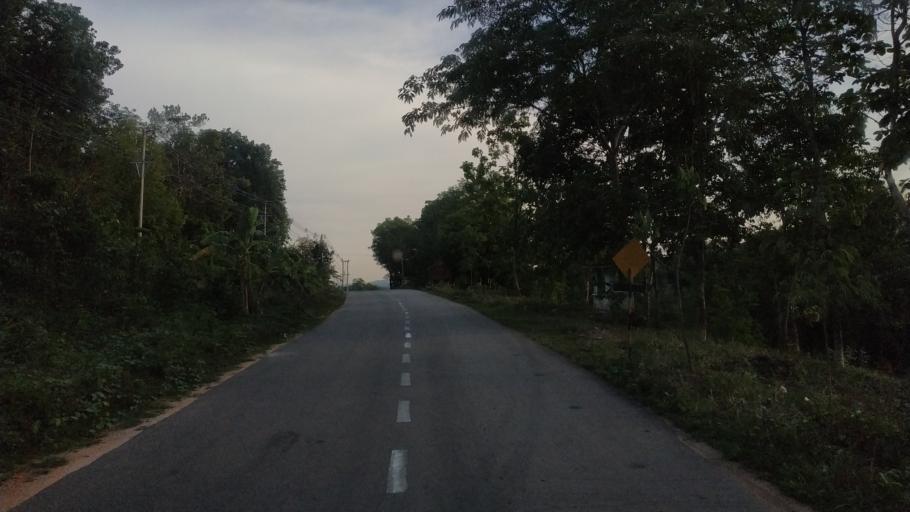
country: MM
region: Mon
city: Kyaikto
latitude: 17.4211
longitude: 97.0721
